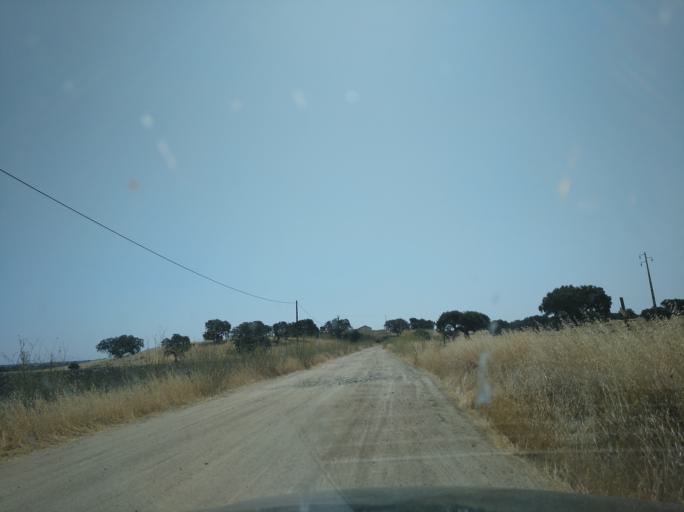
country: PT
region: Portalegre
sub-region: Campo Maior
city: Campo Maior
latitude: 39.0315
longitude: -6.9809
